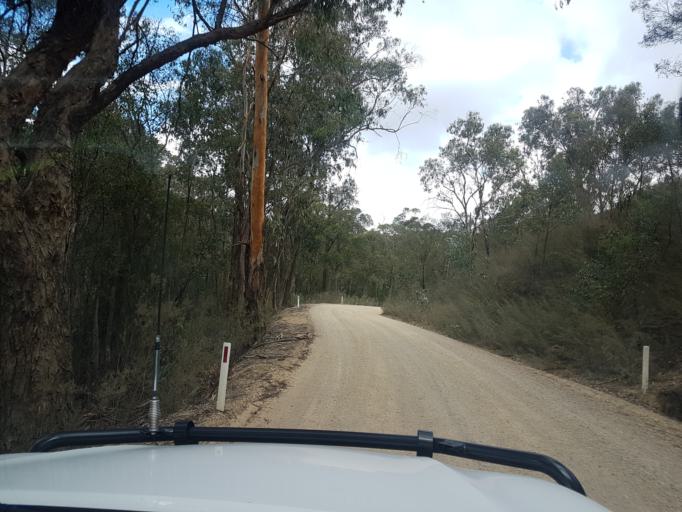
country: AU
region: Victoria
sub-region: East Gippsland
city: Bairnsdale
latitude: -37.6936
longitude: 147.5645
